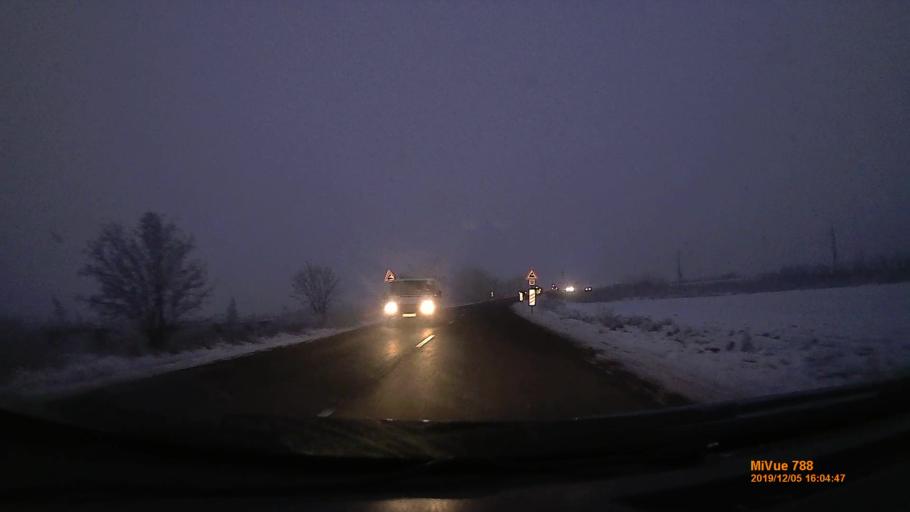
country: HU
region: Borsod-Abauj-Zemplen
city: Tarcal
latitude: 48.1112
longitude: 21.3524
